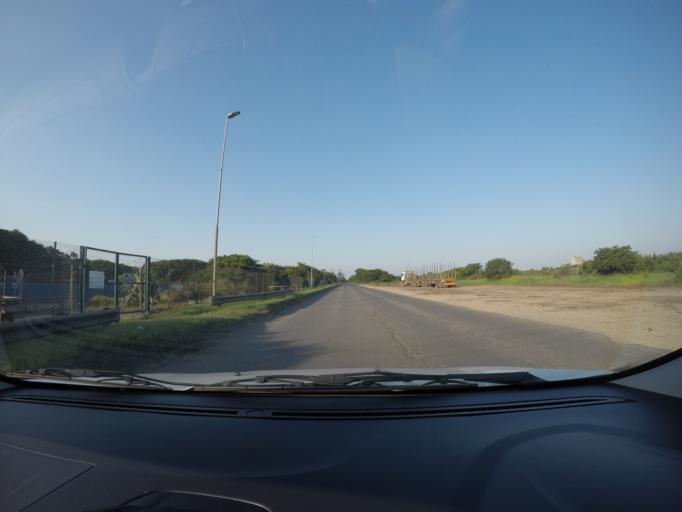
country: ZA
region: KwaZulu-Natal
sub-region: uThungulu District Municipality
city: Richards Bay
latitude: -28.7622
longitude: 32.0012
